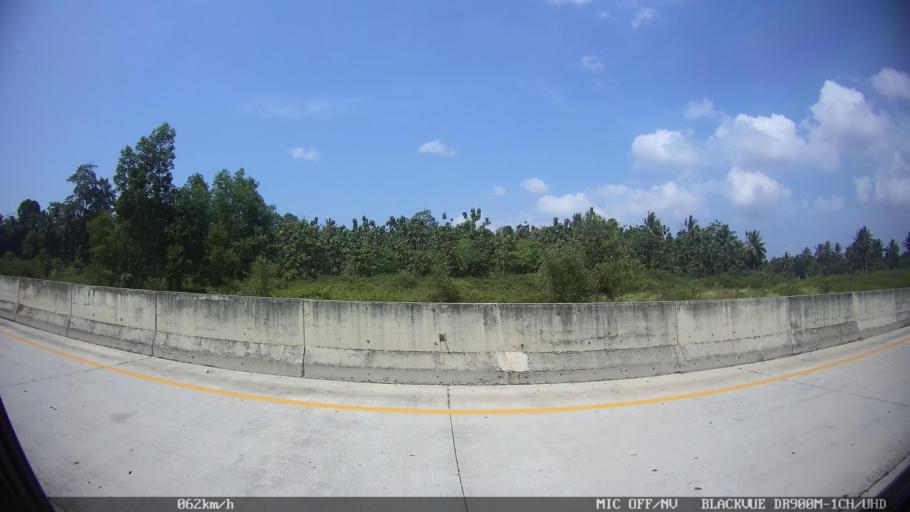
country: ID
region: Lampung
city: Natar
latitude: -5.3136
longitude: 105.2569
